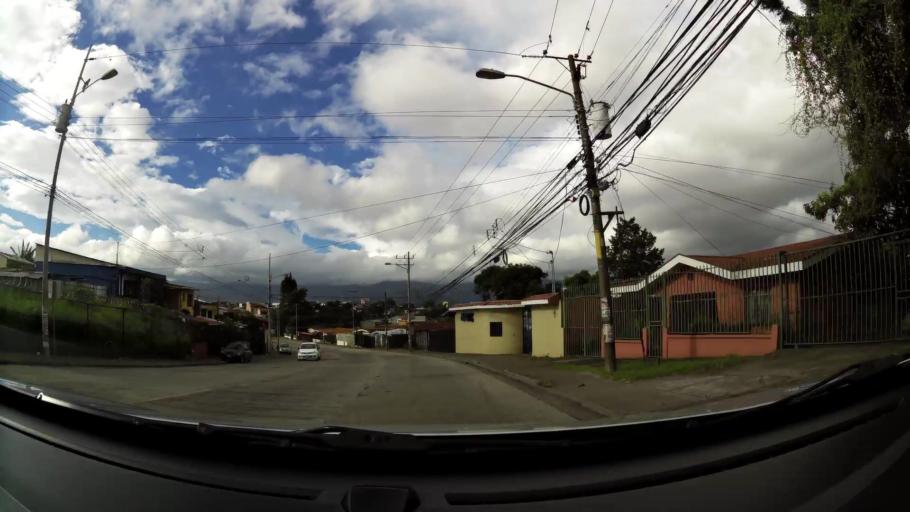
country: CR
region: San Jose
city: San Pedro
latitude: 9.9152
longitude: -84.0558
